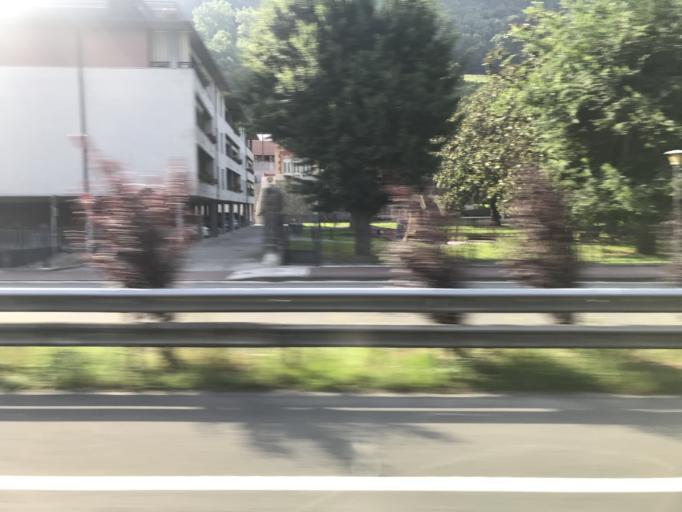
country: ES
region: Basque Country
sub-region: Provincia de Guipuzcoa
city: Irura
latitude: 43.1740
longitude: -2.0591
